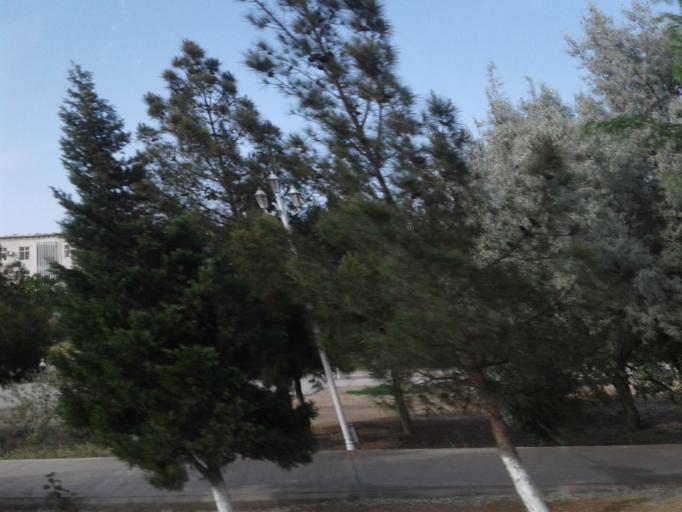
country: TM
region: Balkan
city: Turkmenbasy
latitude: 40.0013
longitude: 52.9561
